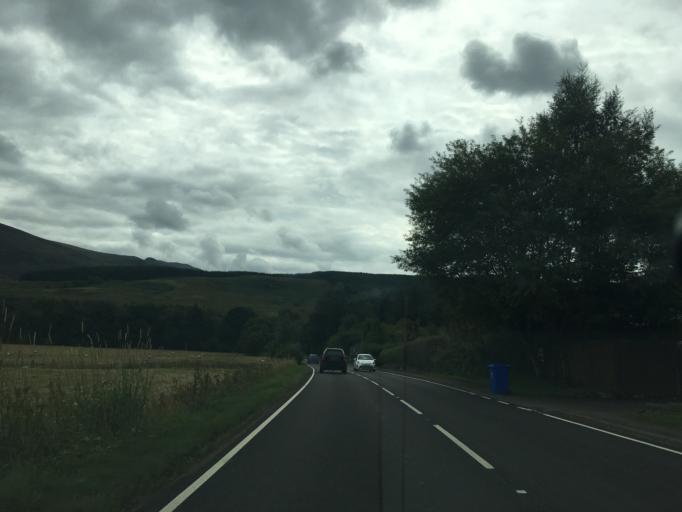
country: GB
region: Scotland
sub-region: Stirling
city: Callander
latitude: 56.3814
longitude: -4.2869
